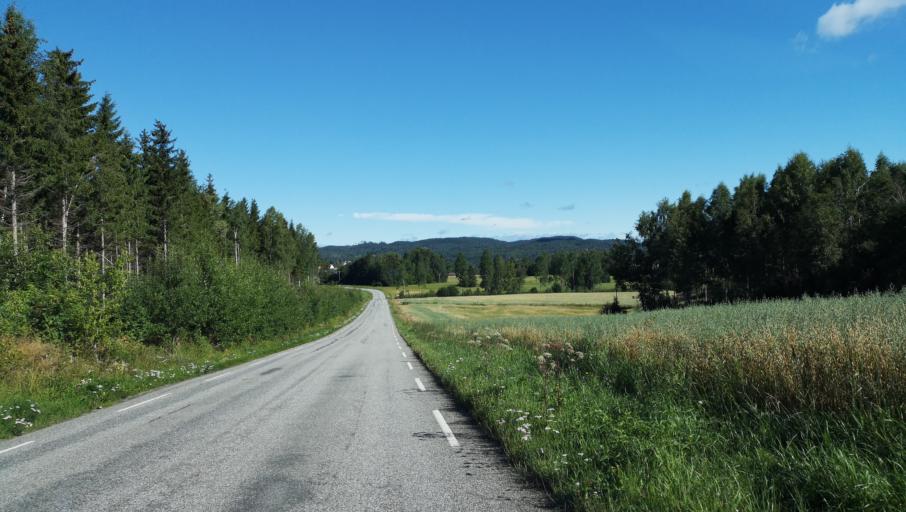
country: NO
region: Ostfold
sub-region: Hobol
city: Tomter
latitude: 59.6452
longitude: 11.0149
